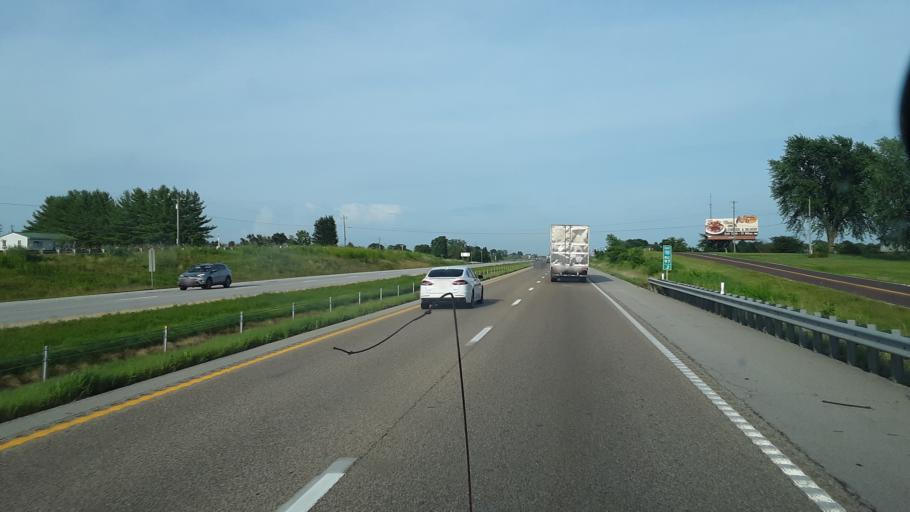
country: US
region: Missouri
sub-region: Cooper County
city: Boonville
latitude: 38.9348
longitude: -92.8630
